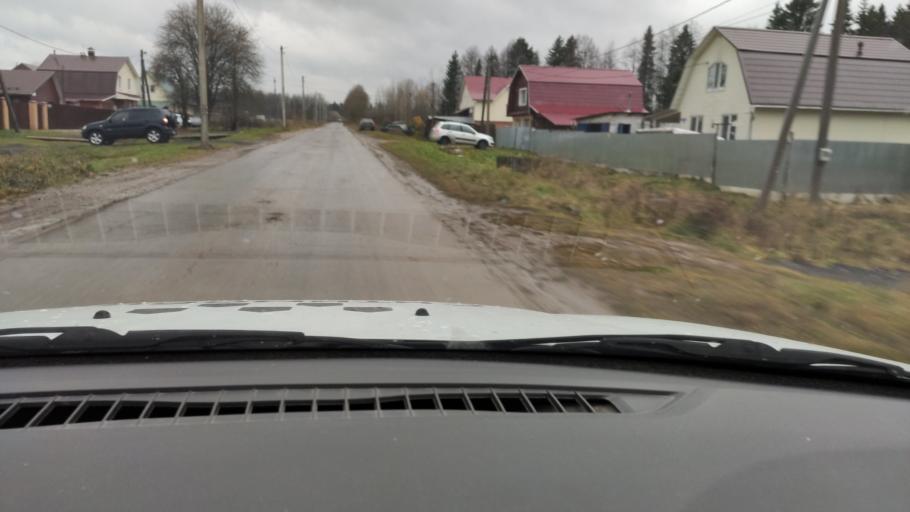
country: RU
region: Perm
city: Sylva
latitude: 58.0381
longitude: 56.7435
